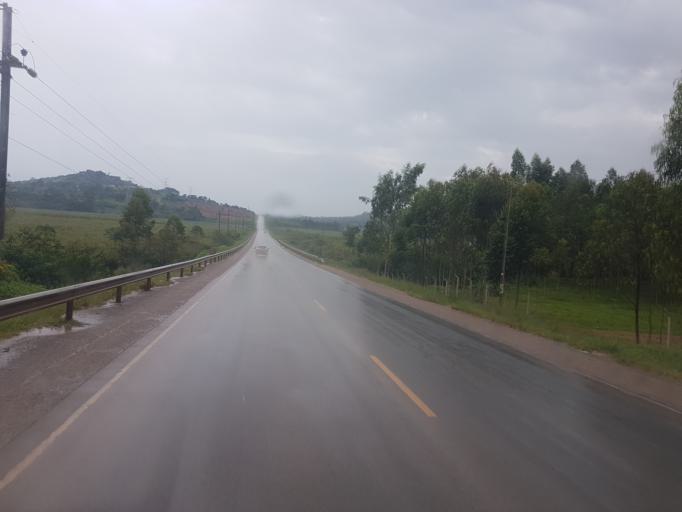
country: UG
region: Central Region
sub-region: Mpigi District
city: Mpigi
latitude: 0.1874
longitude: 32.2903
